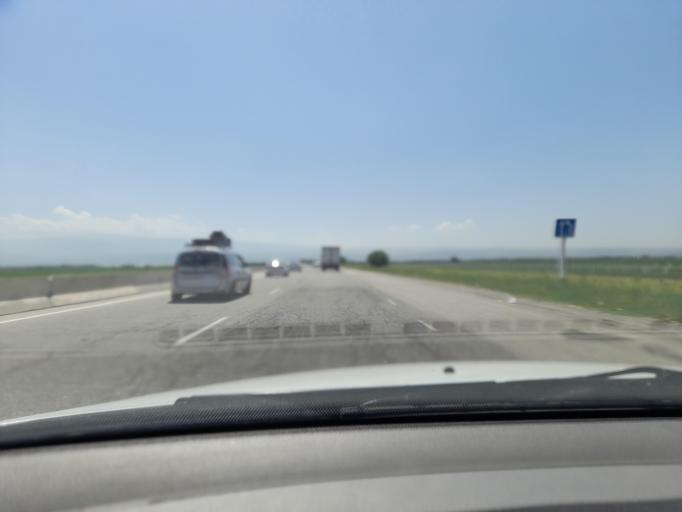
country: UZ
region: Jizzax
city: Jizzax
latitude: 40.1224
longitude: 67.9494
